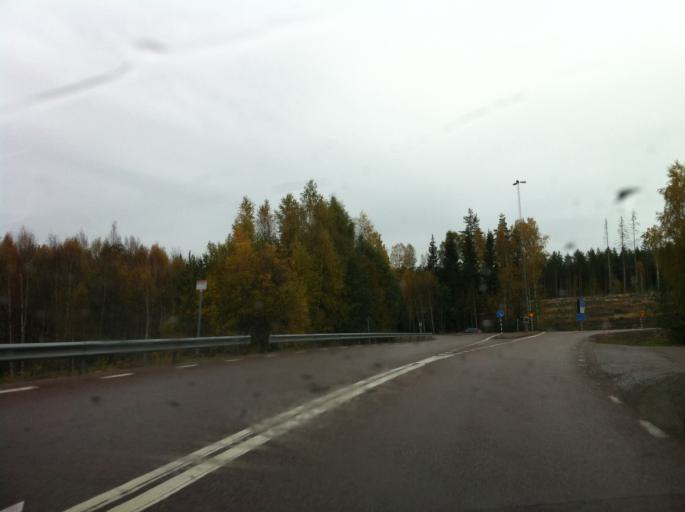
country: SE
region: Dalarna
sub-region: Ludvika Kommun
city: Grangesberg
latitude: 60.2263
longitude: 14.9826
